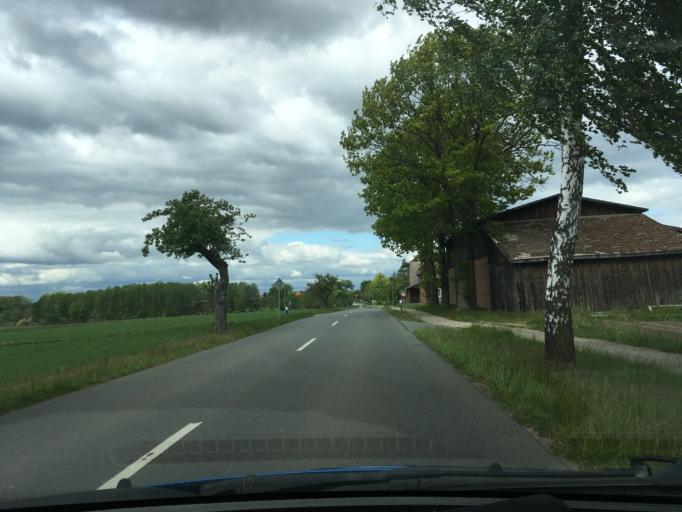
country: DE
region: Lower Saxony
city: Gerdau
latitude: 52.9170
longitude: 10.4178
